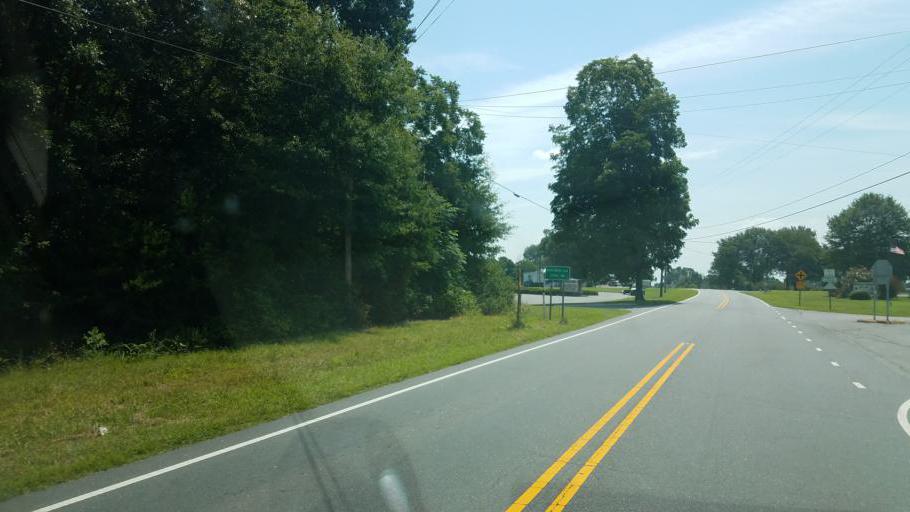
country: US
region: North Carolina
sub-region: Gaston County
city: Cherryville
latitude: 35.5095
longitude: -81.4582
